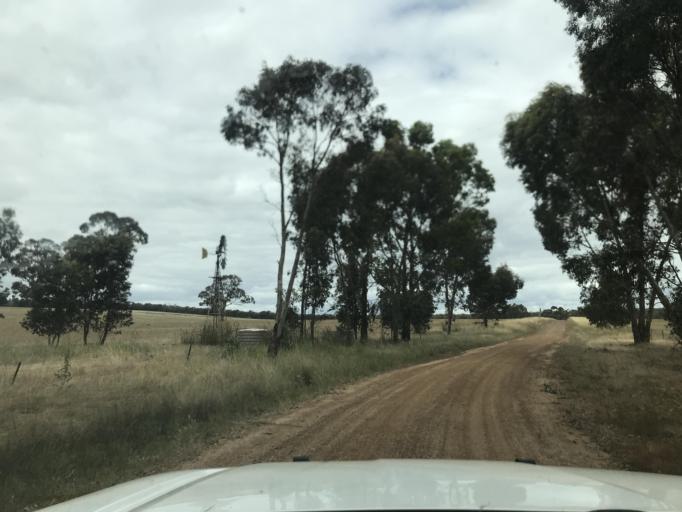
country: AU
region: South Australia
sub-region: Naracoorte and Lucindale
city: Naracoorte
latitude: -36.9212
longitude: 141.3169
